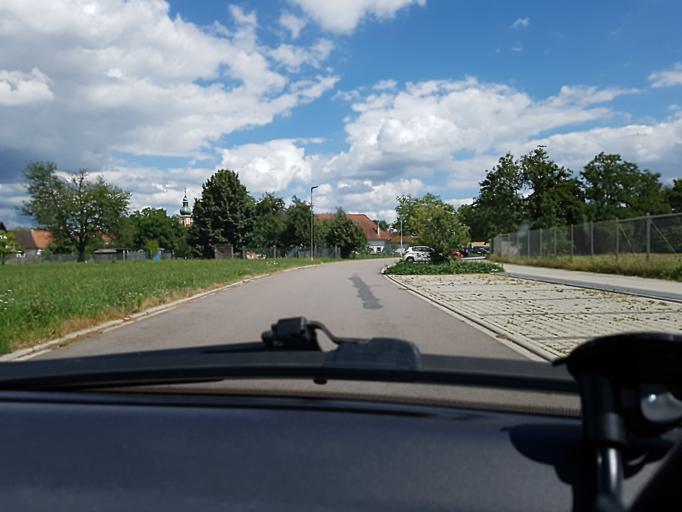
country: DE
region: Baden-Wuerttemberg
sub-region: Freiburg Region
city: Willstatt
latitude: 48.5419
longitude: 7.8879
